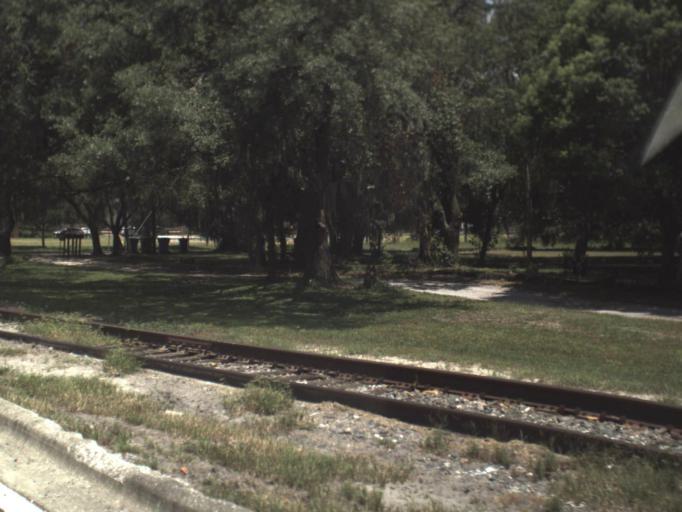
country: US
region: Florida
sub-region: Hillsborough County
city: Lutz
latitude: 28.1308
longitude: -82.4636
